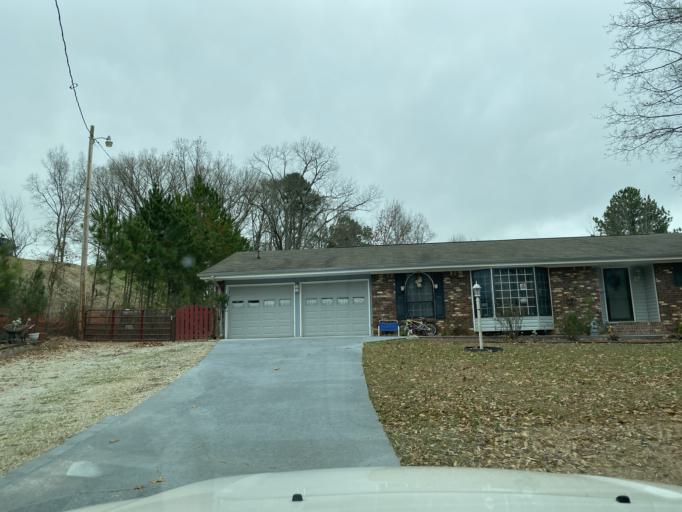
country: US
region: Georgia
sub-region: Cobb County
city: Fair Oaks
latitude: 33.9200
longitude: -84.5847
